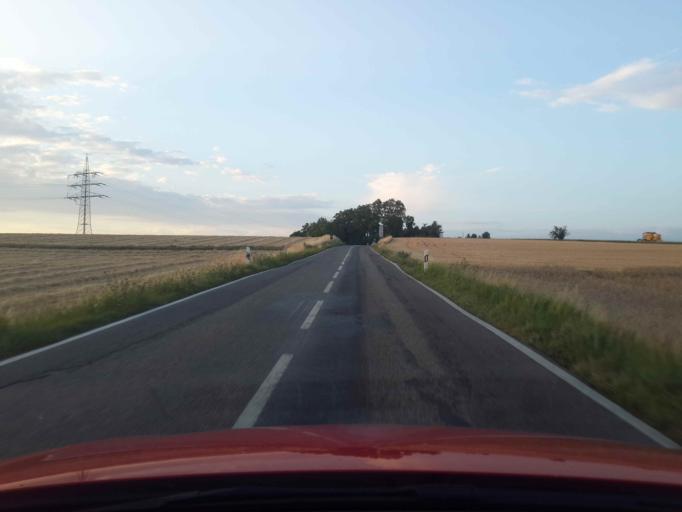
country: DE
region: Baden-Wuerttemberg
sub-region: Regierungsbezirk Stuttgart
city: Nordheim
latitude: 49.1228
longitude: 9.1301
